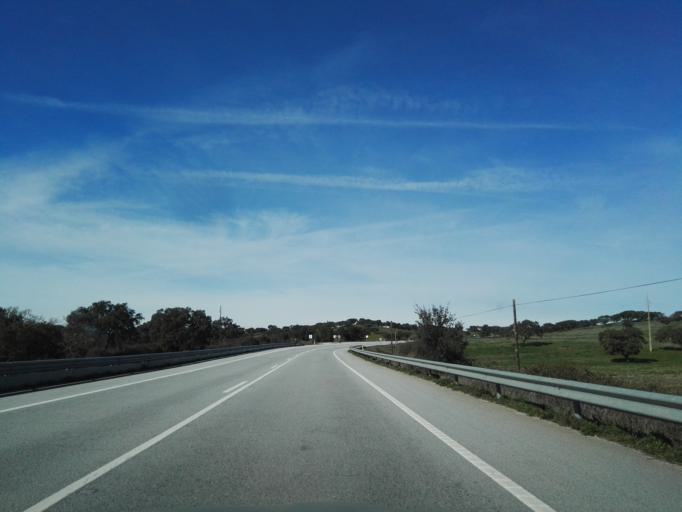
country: PT
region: Portalegre
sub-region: Portalegre
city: Urra
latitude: 39.1962
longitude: -7.3632
